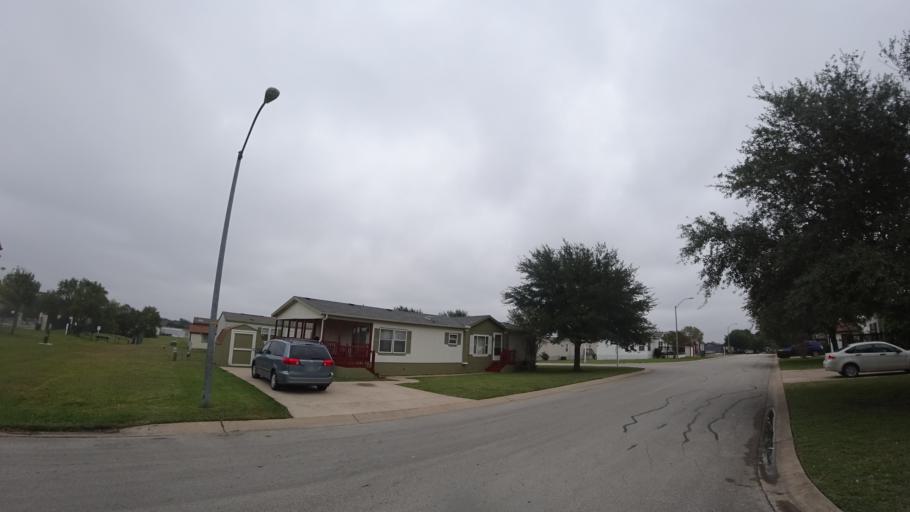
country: US
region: Texas
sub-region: Travis County
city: Pflugerville
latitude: 30.4128
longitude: -97.6052
